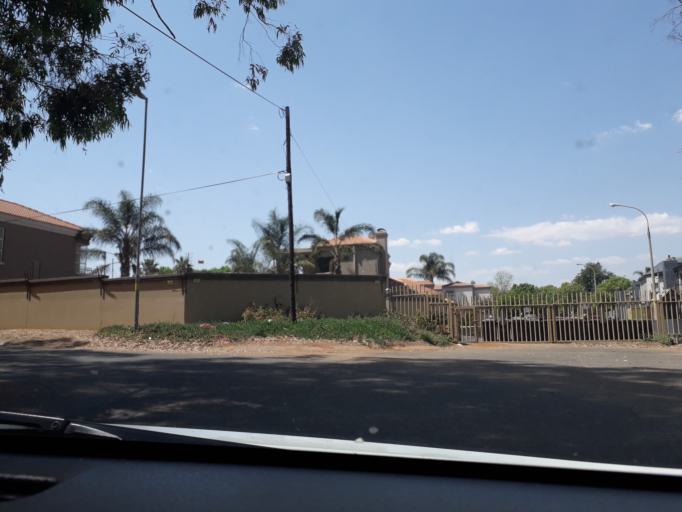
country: ZA
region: Gauteng
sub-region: City of Johannesburg Metropolitan Municipality
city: Modderfontein
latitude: -26.0816
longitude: 28.1996
